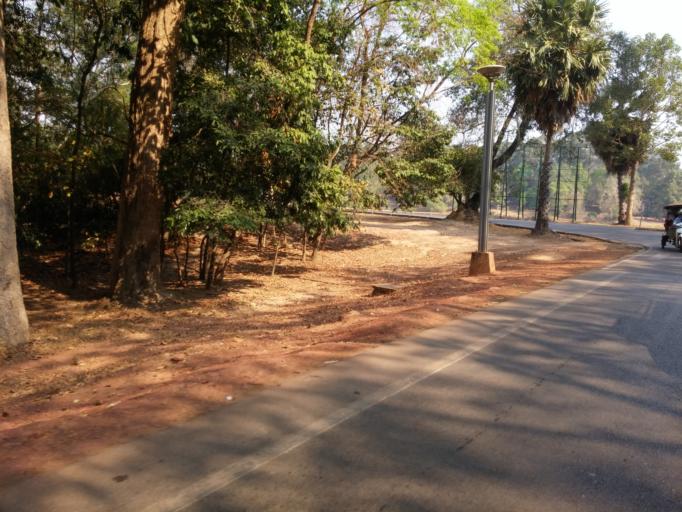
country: KH
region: Siem Reap
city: Siem Reap
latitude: 13.4060
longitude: 103.8666
